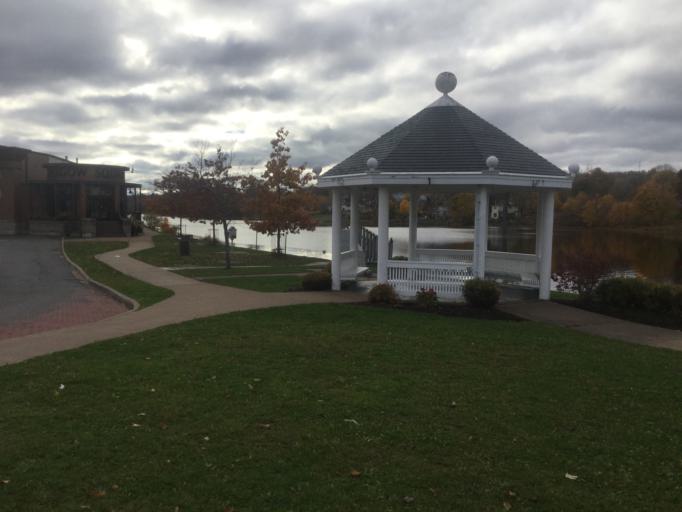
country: CA
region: Nova Scotia
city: New Glasgow
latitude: 45.5882
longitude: -62.6461
